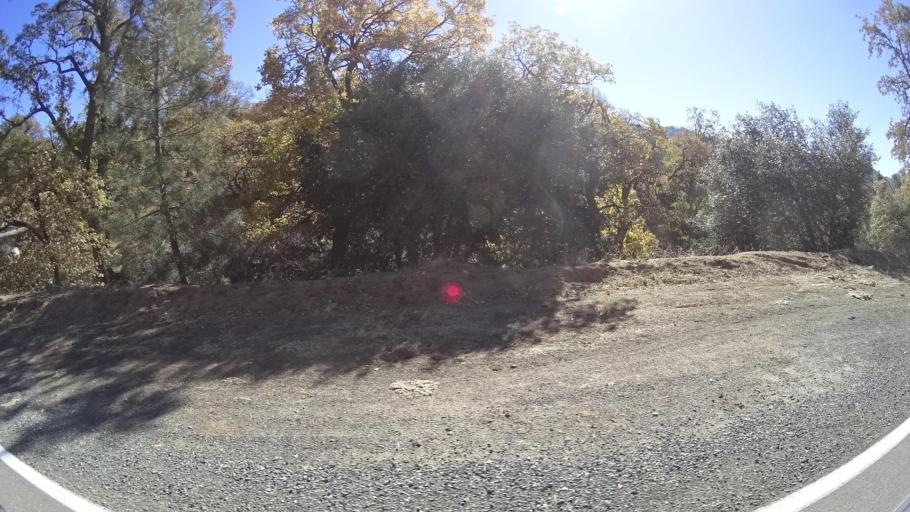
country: US
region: California
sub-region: Kern County
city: Alta Sierra
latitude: 35.7451
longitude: -118.5974
